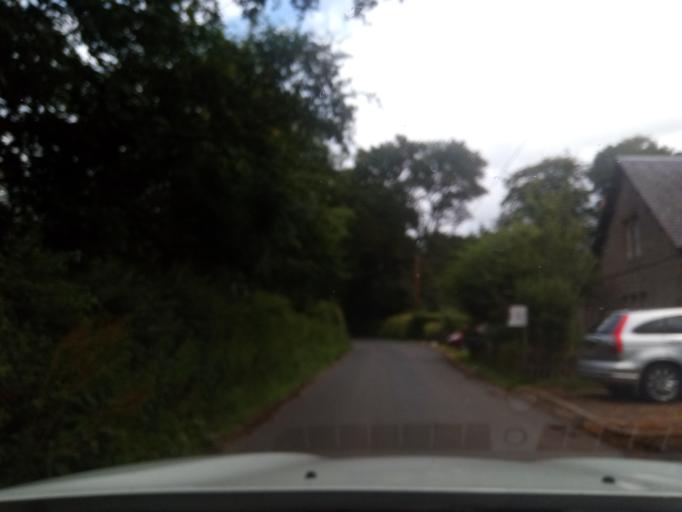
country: GB
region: Scotland
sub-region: The Scottish Borders
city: Jedburgh
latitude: 55.5255
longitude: -2.5170
